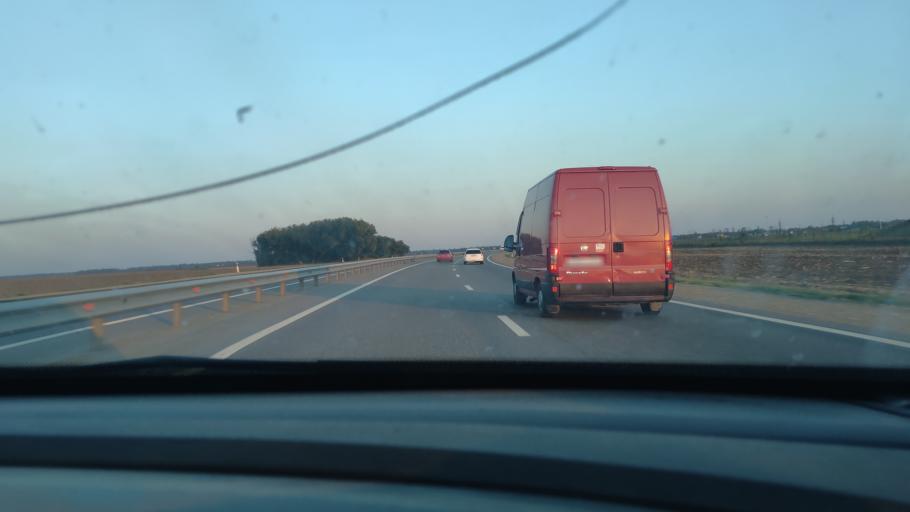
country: RU
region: Krasnodarskiy
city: Timashevsk
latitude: 45.6357
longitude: 38.9767
